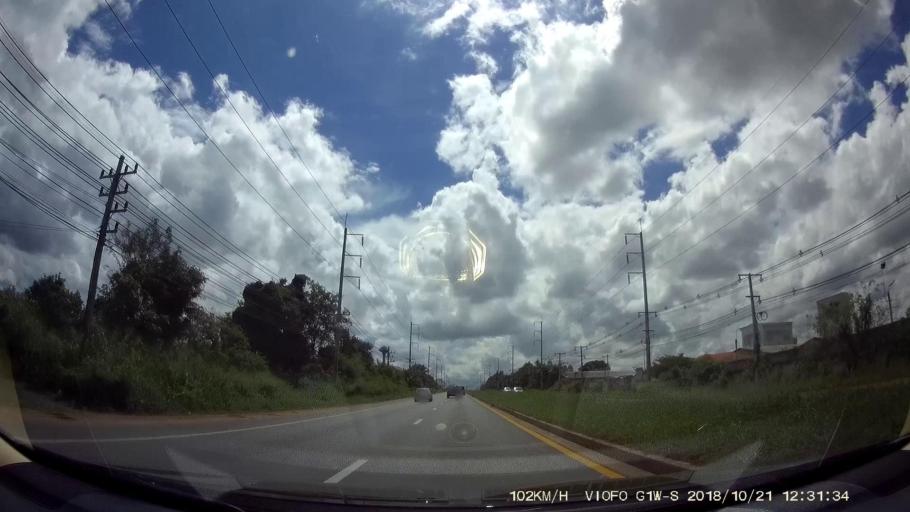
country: TH
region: Nakhon Ratchasima
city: Dan Khun Thot
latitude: 15.1546
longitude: 101.7343
